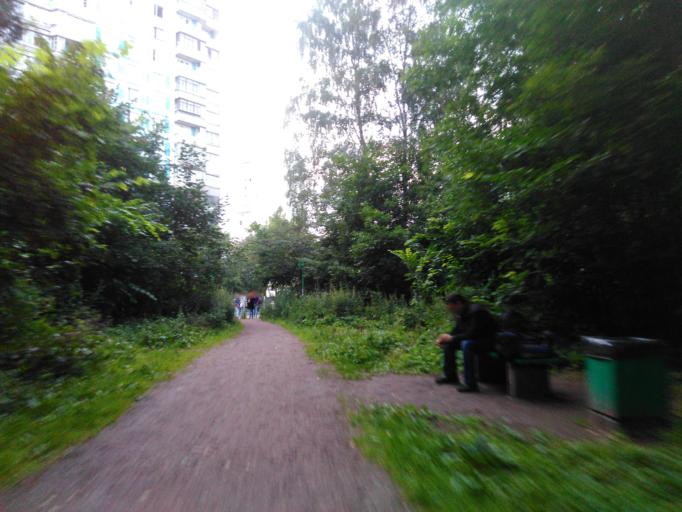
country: RU
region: Moscow
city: Yaroslavskiy
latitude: 55.8688
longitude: 37.7144
